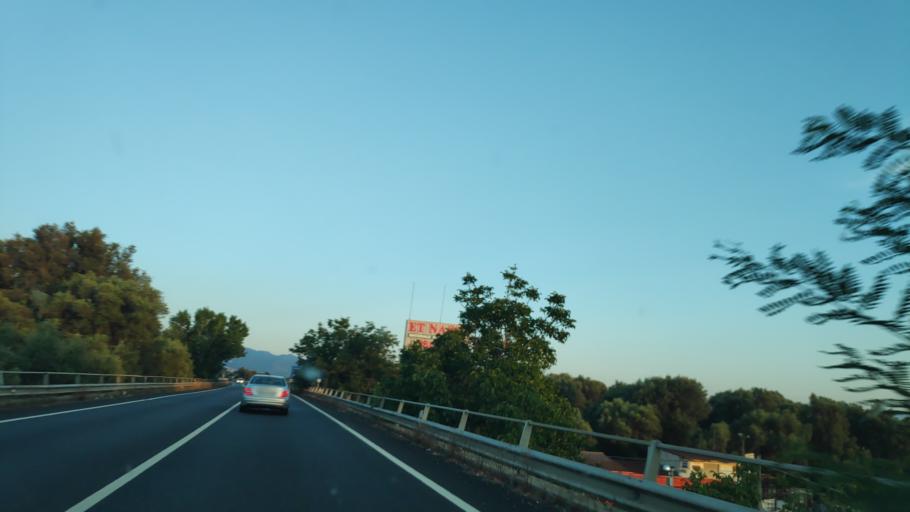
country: IT
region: Calabria
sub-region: Provincia di Reggio Calabria
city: Melicucco
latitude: 38.4350
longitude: 16.0487
